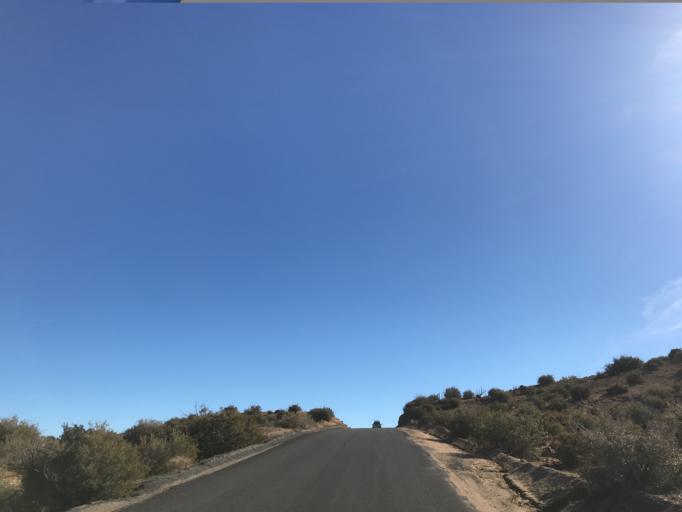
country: US
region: California
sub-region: San Bernardino County
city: Yucca Valley
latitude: 34.1888
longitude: -116.5451
